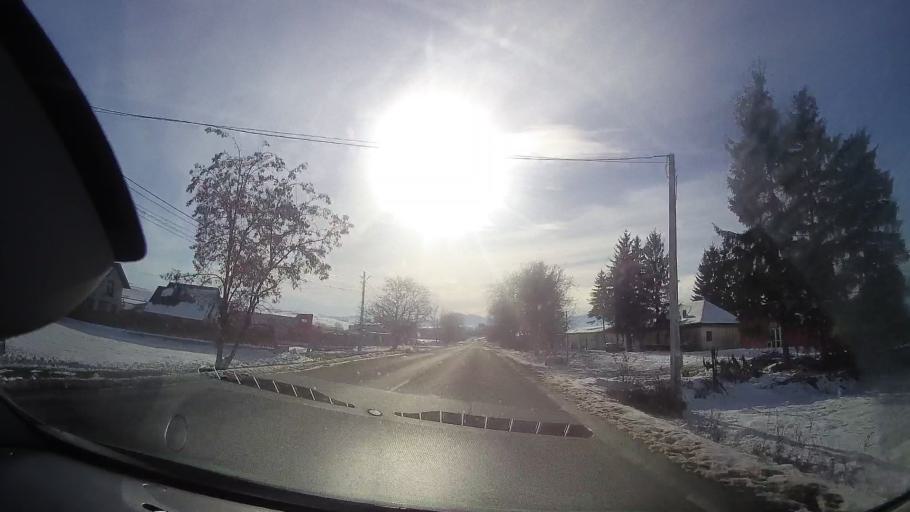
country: RO
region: Neamt
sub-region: Comuna Baltatesti
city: Valea Seaca
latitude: 47.1432
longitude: 26.3191
